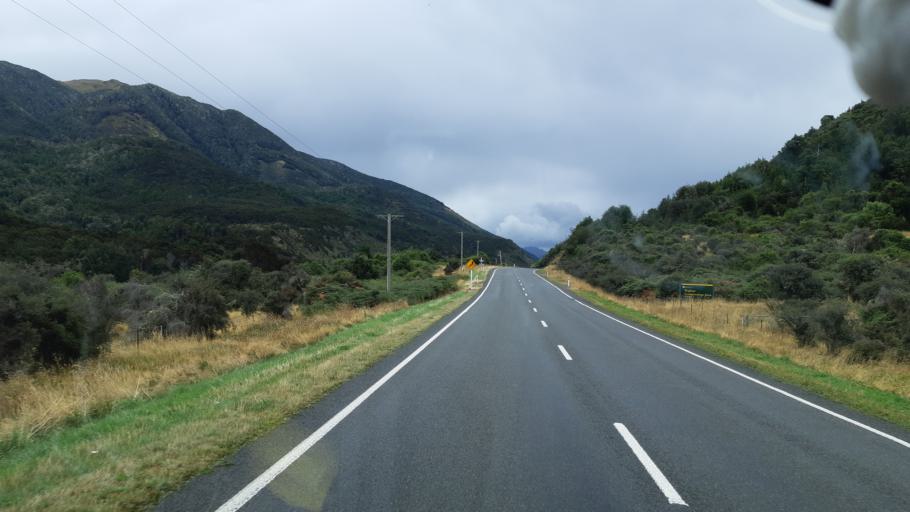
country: NZ
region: Canterbury
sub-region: Hurunui District
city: Amberley
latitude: -42.5723
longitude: 172.3686
